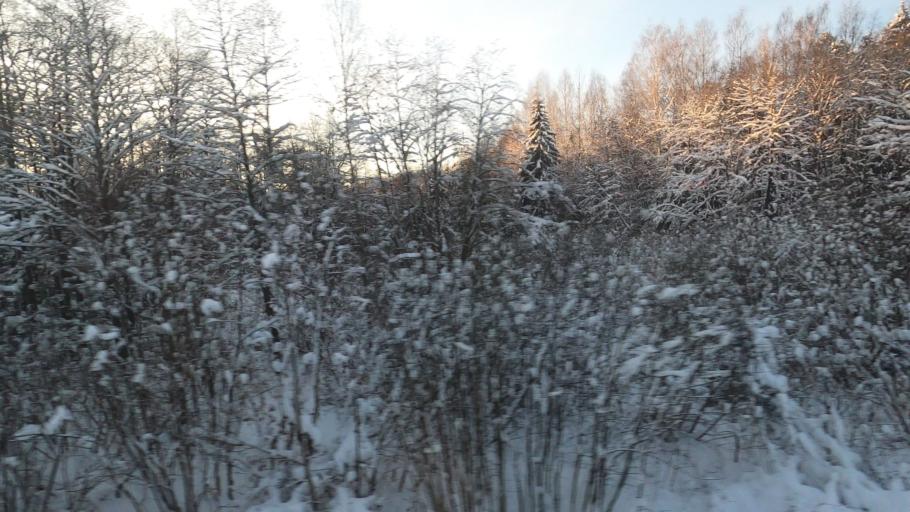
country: RU
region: Moskovskaya
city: Novo-Nikol'skoye
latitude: 56.6110
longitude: 37.5675
